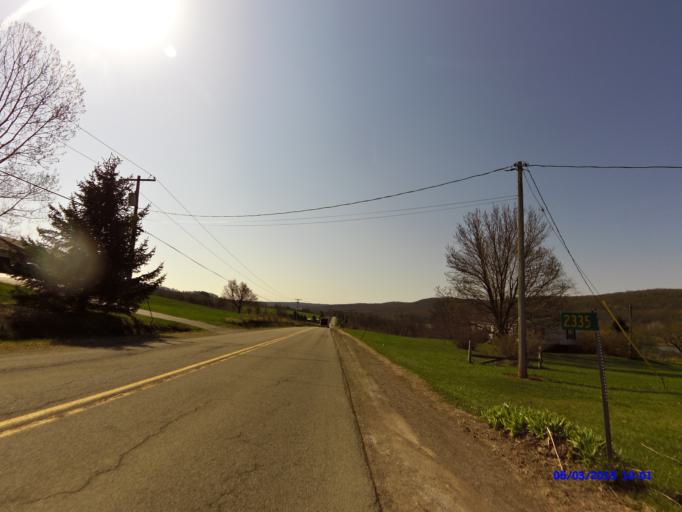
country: US
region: New York
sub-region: Cattaraugus County
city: Franklinville
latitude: 42.3276
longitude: -78.4381
